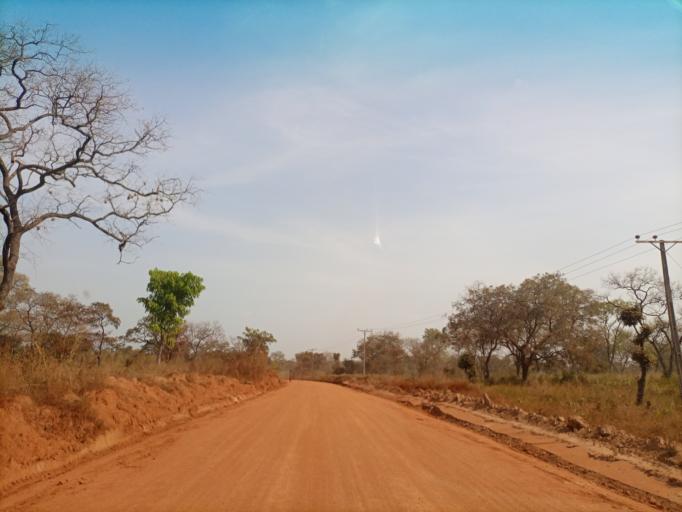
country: NG
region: Enugu
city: Eha Amufu
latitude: 6.6699
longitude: 7.7401
